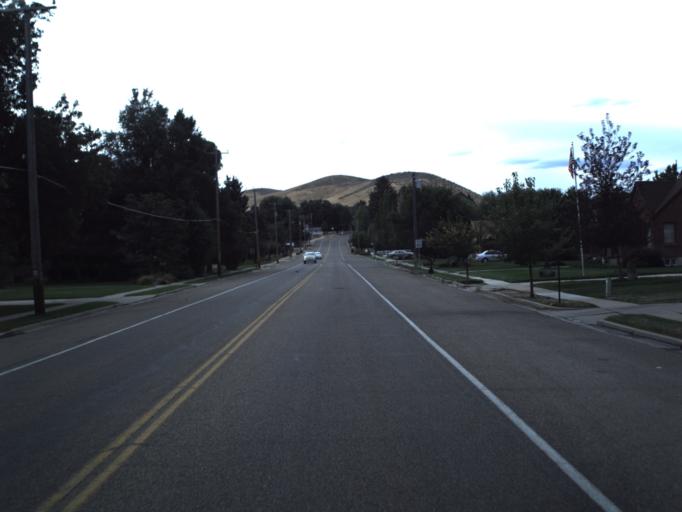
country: US
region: Utah
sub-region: Morgan County
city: Morgan
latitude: 41.0337
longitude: -111.6762
